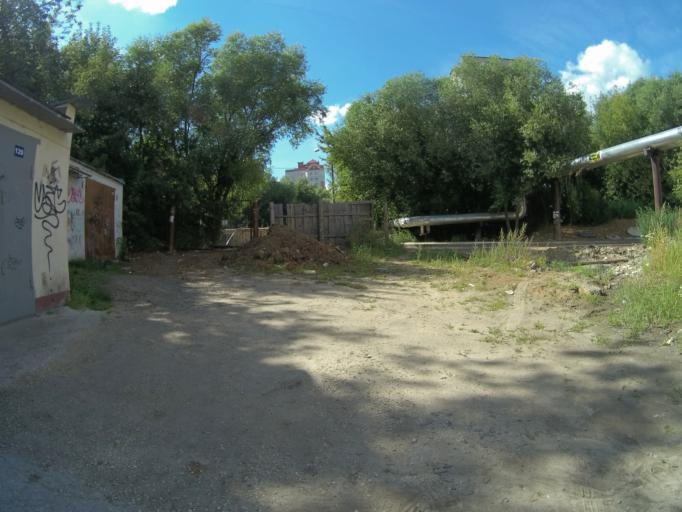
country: RU
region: Vladimir
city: Vladimir
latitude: 56.1366
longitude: 40.3717
